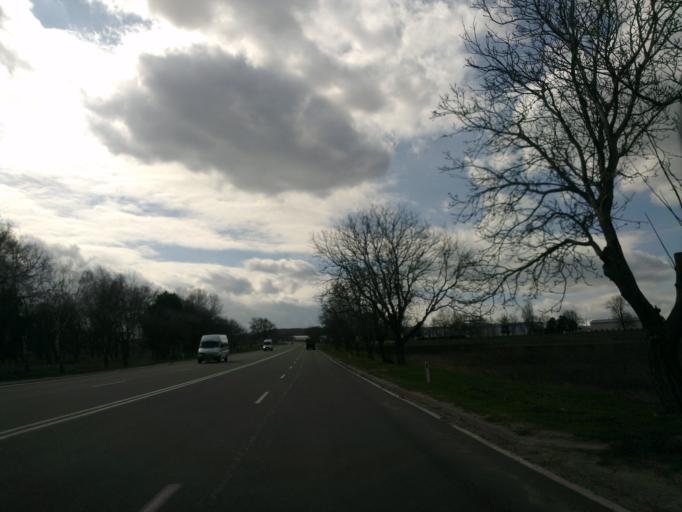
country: MD
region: Laloveni
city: Ialoveni
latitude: 46.9502
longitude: 28.7225
